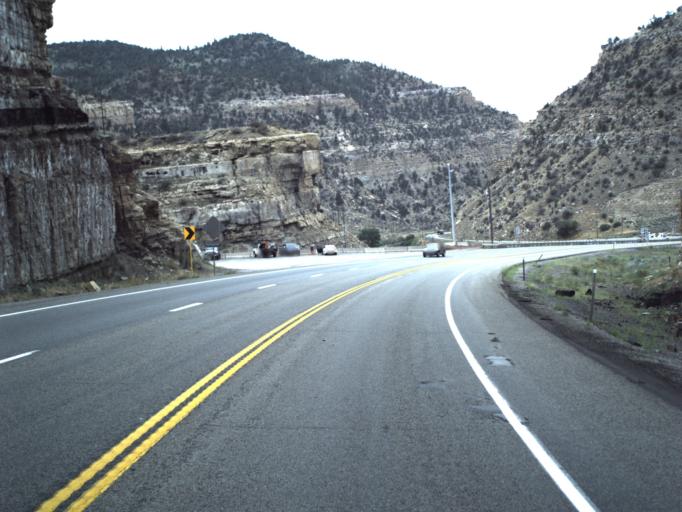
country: US
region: Utah
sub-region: Carbon County
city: Helper
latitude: 39.7286
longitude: -110.8678
